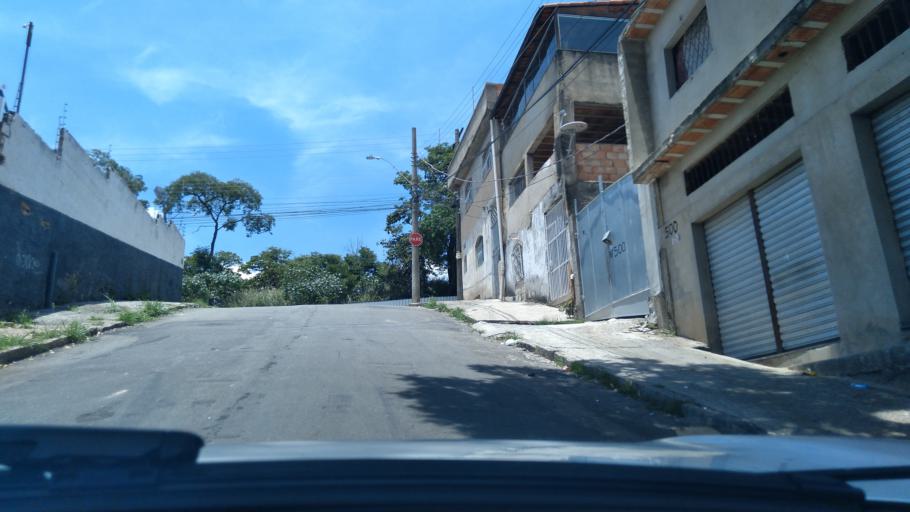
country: BR
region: Minas Gerais
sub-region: Contagem
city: Contagem
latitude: -19.9280
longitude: -44.0135
